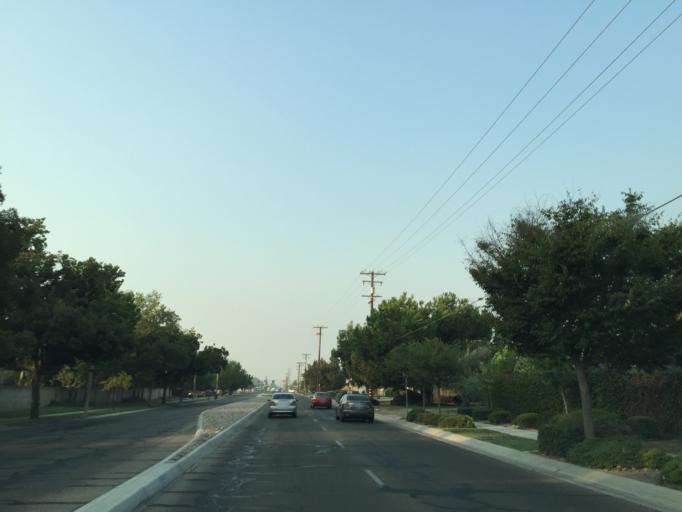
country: US
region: California
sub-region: Tulare County
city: Visalia
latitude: 36.3454
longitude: -119.2789
